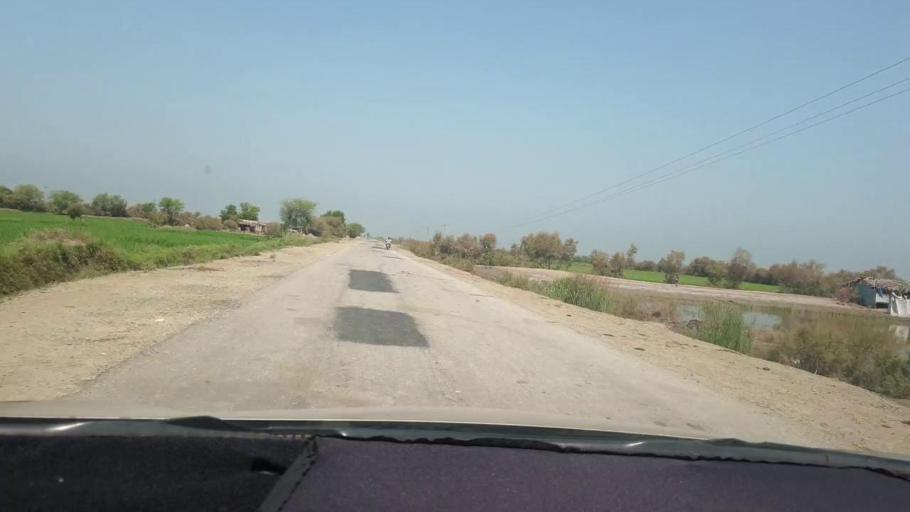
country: PK
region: Sindh
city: Miro Khan
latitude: 27.8264
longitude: 68.0186
